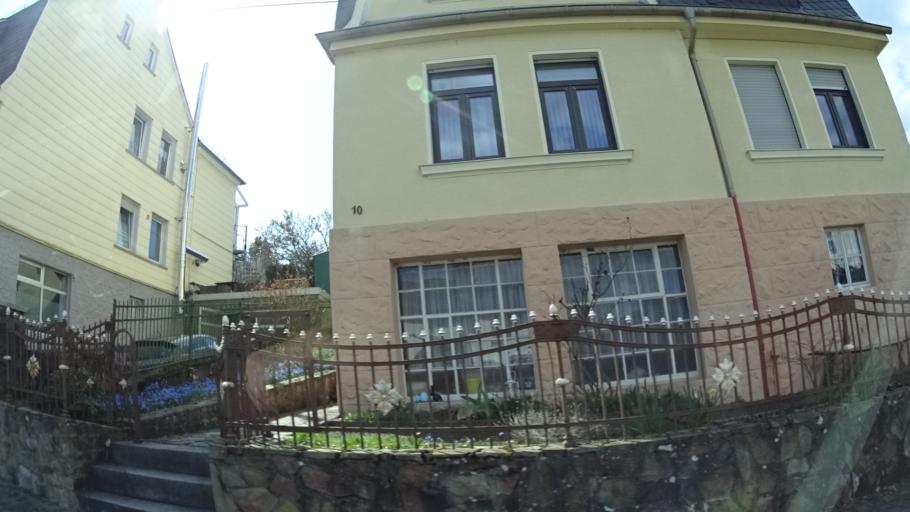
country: DE
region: Rheinland-Pfalz
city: Kirschweiler
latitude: 49.7576
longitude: 7.2409
